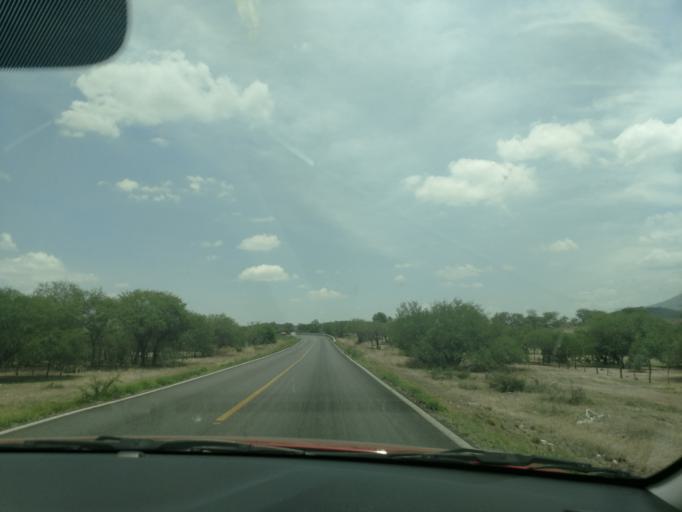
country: MX
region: San Luis Potosi
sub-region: Rioverde
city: Progreso
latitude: 22.0170
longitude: -100.3632
